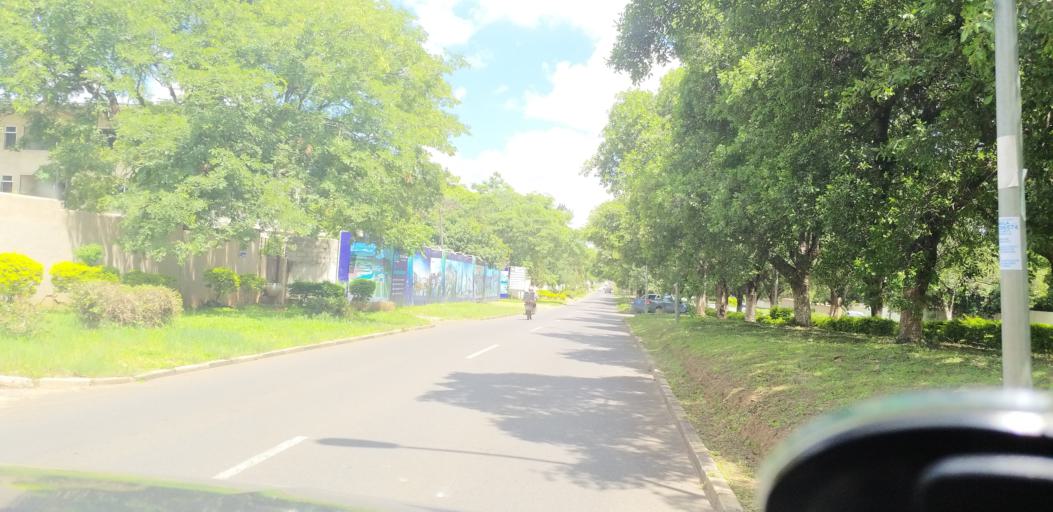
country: ZM
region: Lusaka
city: Lusaka
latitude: -15.4277
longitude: 28.3188
